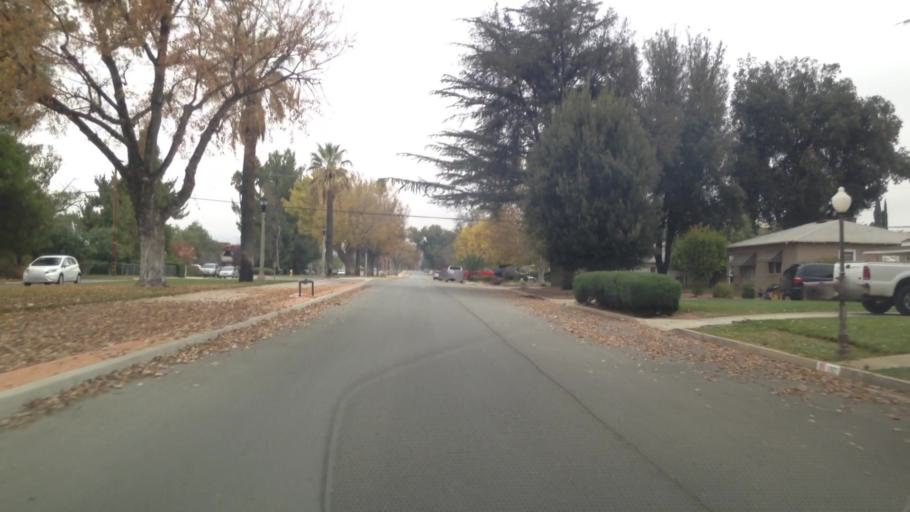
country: US
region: California
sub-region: Riverside County
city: Beaumont
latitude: 33.9364
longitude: -116.9716
